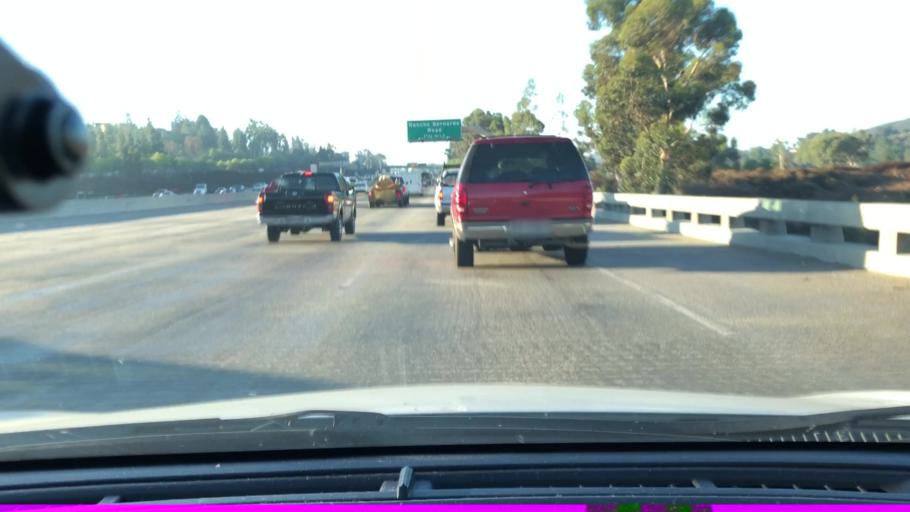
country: US
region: California
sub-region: San Diego County
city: Escondido
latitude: 33.0427
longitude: -117.0744
